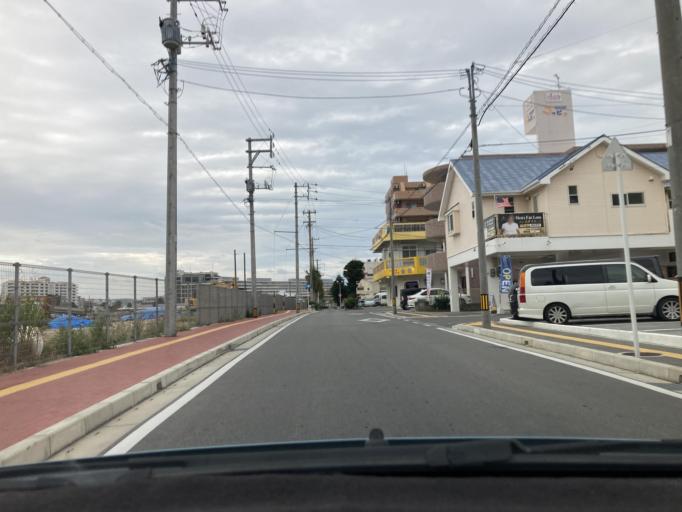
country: JP
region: Okinawa
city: Chatan
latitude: 26.3233
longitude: 127.7513
